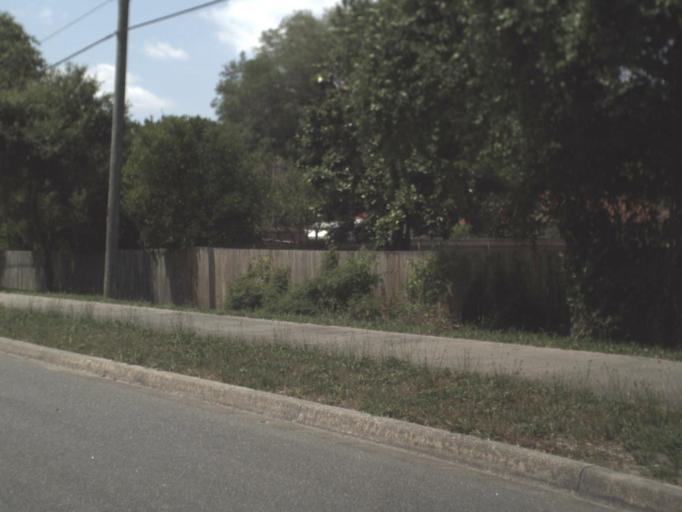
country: US
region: Florida
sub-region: Duval County
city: Atlantic Beach
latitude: 30.3599
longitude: -81.4178
